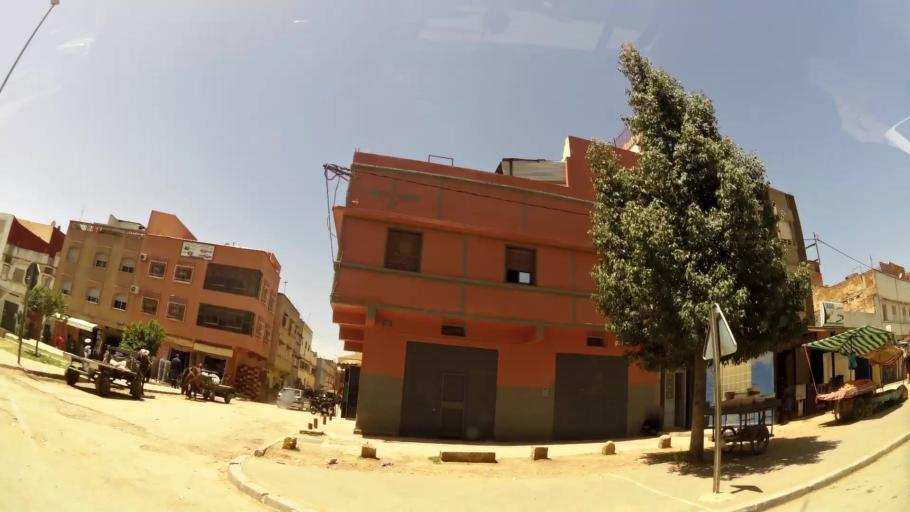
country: MA
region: Rabat-Sale-Zemmour-Zaer
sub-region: Khemisset
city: Khemisset
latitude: 33.8340
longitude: -6.0658
